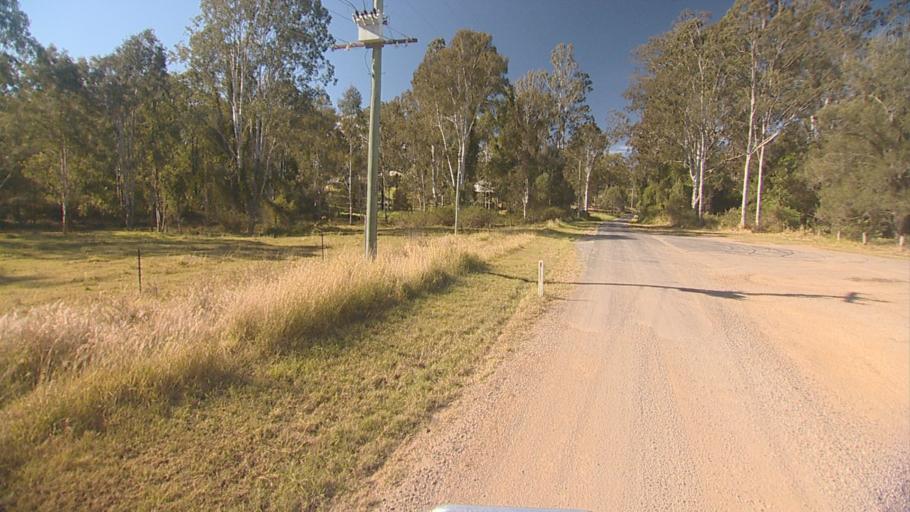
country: AU
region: Queensland
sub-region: Ipswich
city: Springfield Lakes
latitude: -27.7452
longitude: 152.9156
